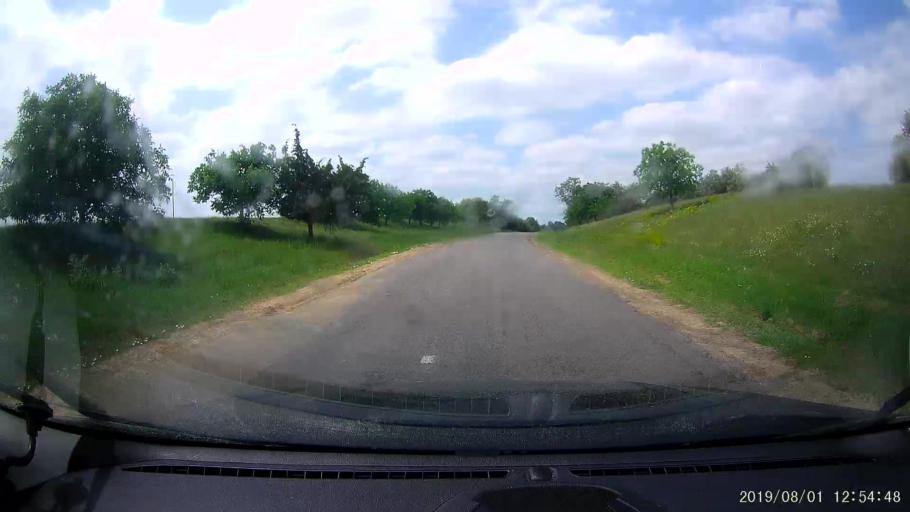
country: MD
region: Gagauzia
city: Vulcanesti
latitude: 45.6948
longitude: 28.4801
